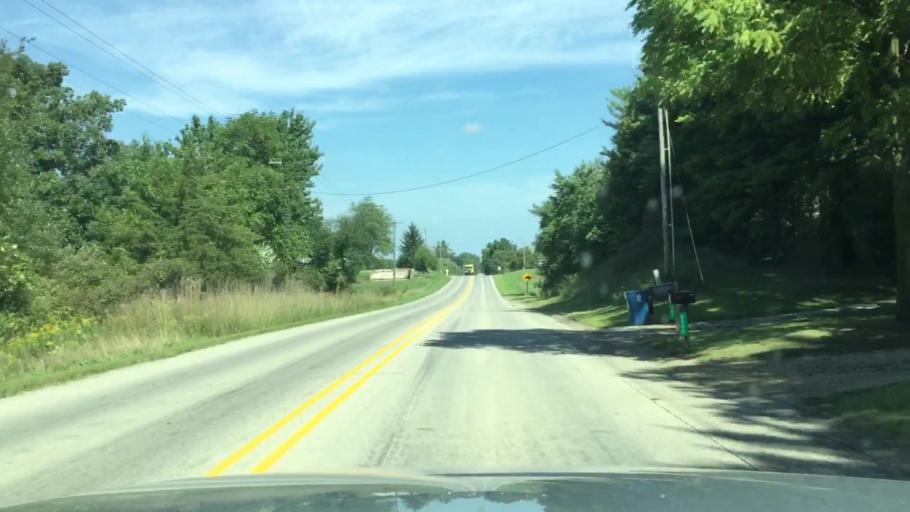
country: US
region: Michigan
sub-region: Lenawee County
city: Manitou Beach-Devils Lake
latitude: 42.0146
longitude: -84.2762
